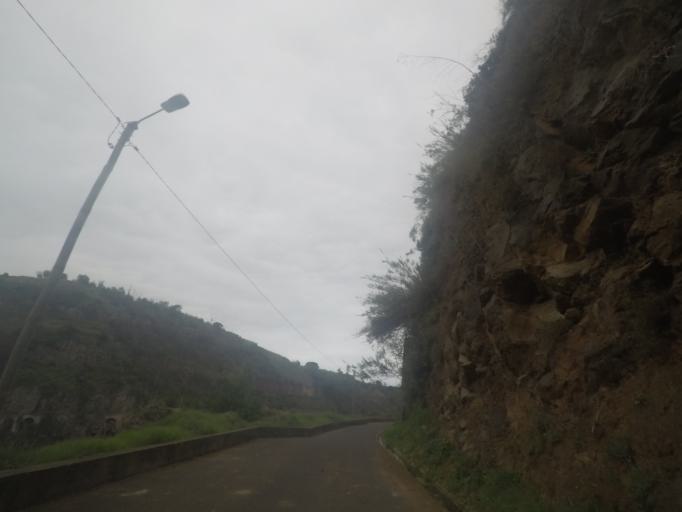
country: PT
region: Madeira
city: Camara de Lobos
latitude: 32.6616
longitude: -16.9621
